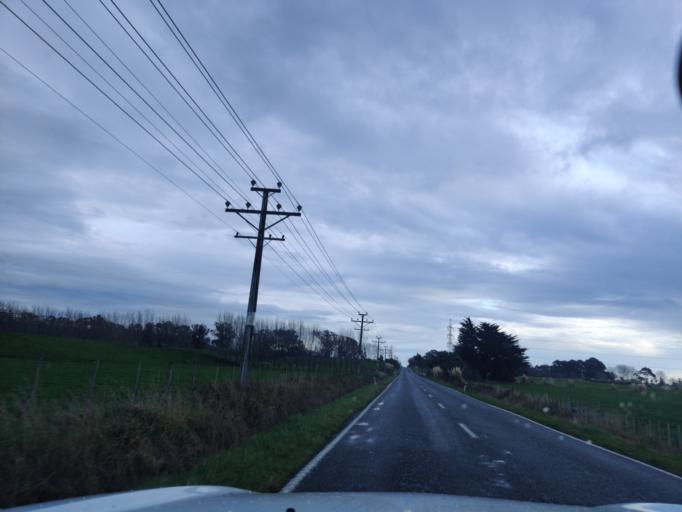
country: NZ
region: Manawatu-Wanganui
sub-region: Palmerston North City
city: Palmerston North
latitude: -40.3415
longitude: 175.7162
